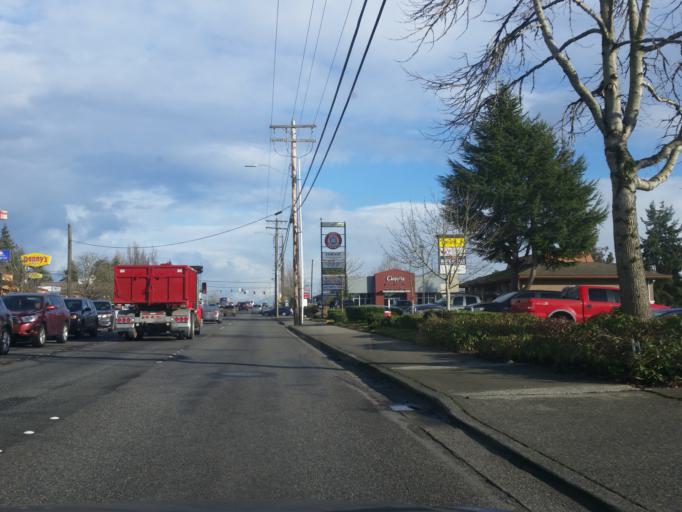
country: US
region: Washington
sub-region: Snohomish County
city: Alderwood Manor
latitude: 47.8209
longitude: -122.2907
